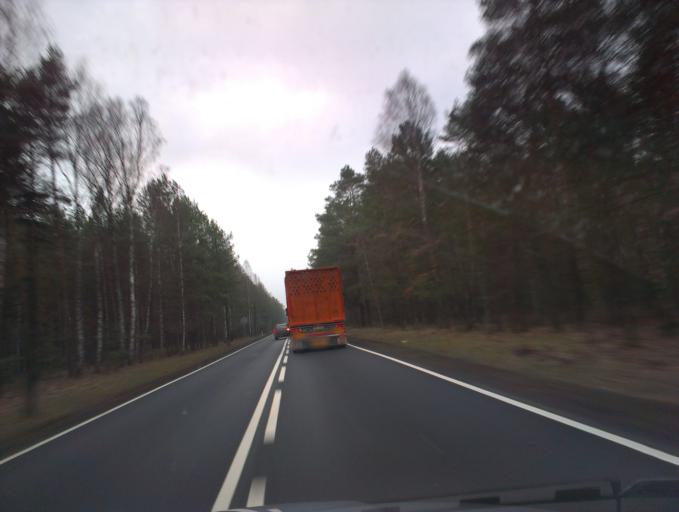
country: PL
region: Greater Poland Voivodeship
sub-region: Powiat zlotowski
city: Tarnowka
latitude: 53.2745
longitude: 16.7816
